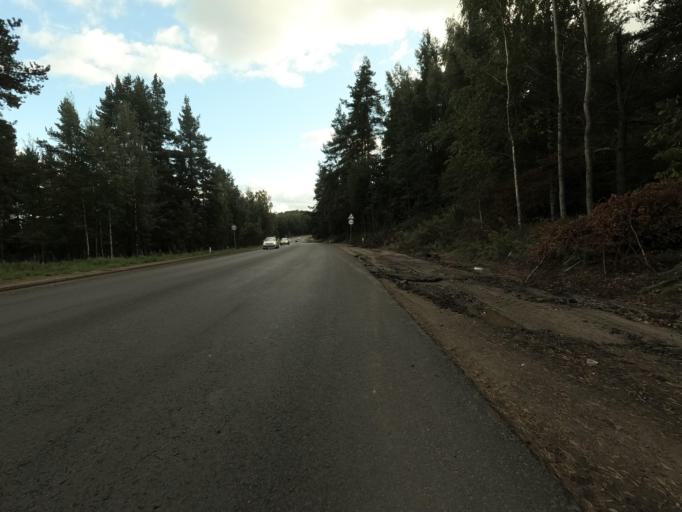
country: RU
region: Leningrad
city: Koltushi
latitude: 59.9609
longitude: 30.6584
